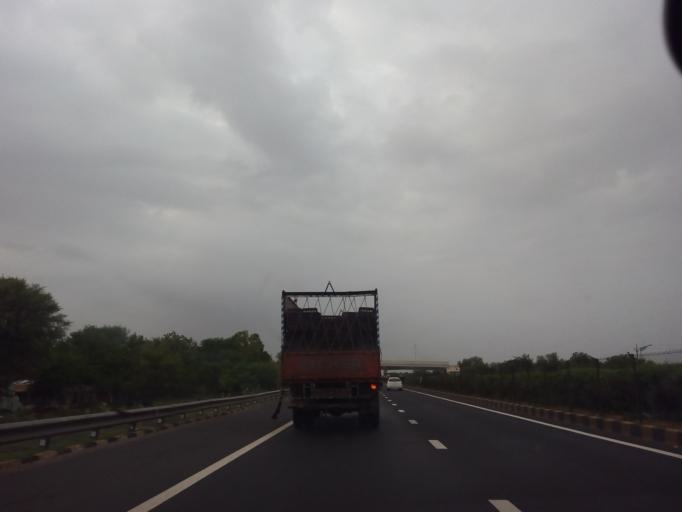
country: IN
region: Gujarat
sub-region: Kheda
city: Mahemdavad
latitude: 22.8605
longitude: 72.8083
